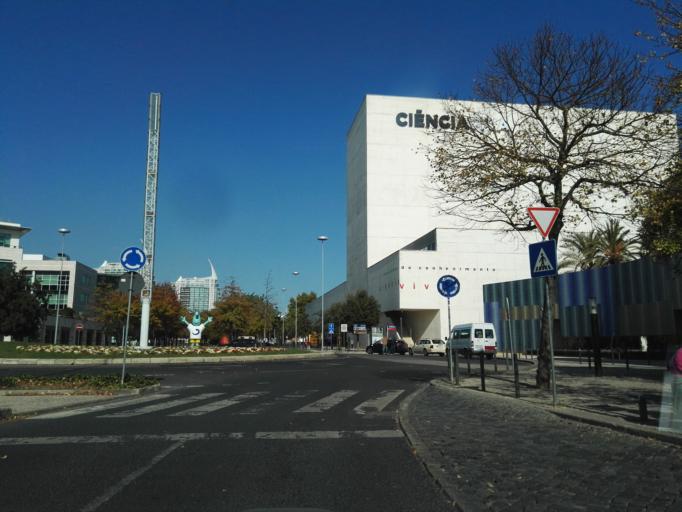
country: PT
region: Lisbon
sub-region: Loures
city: Moscavide
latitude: 38.7612
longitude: -9.0962
